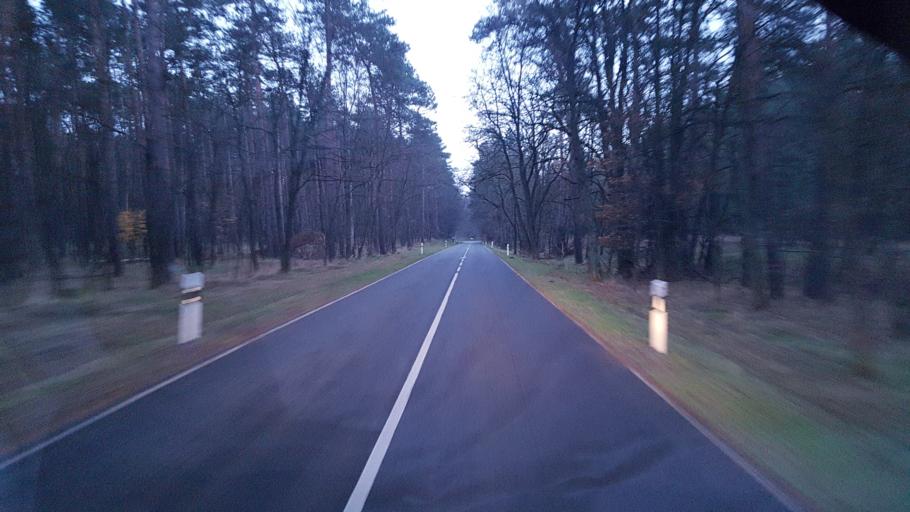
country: DE
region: Brandenburg
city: Jamlitz
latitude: 52.0008
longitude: 14.3691
